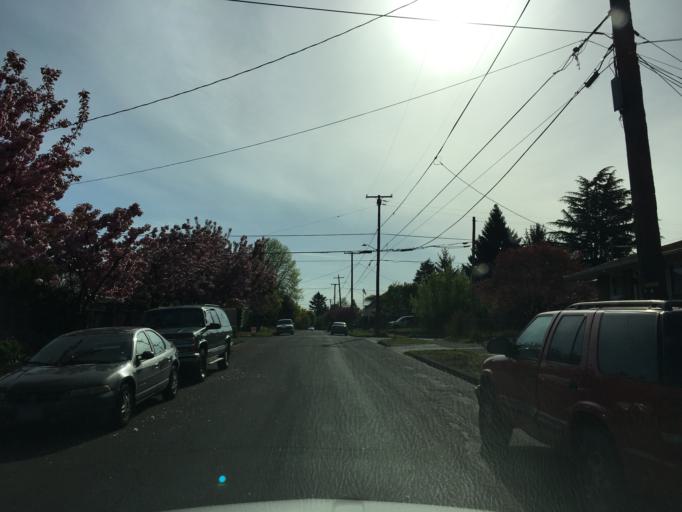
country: US
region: Oregon
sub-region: Multnomah County
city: Lents
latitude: 45.5211
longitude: -122.5786
